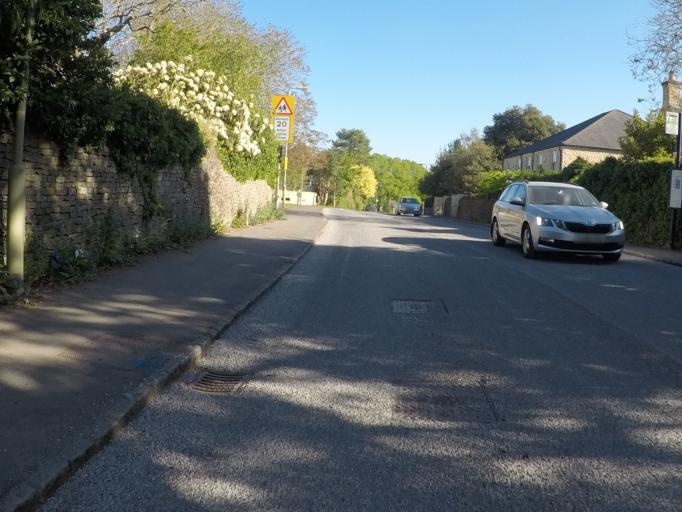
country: GB
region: England
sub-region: Oxfordshire
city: Charlbury
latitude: 51.8747
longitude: -1.4768
